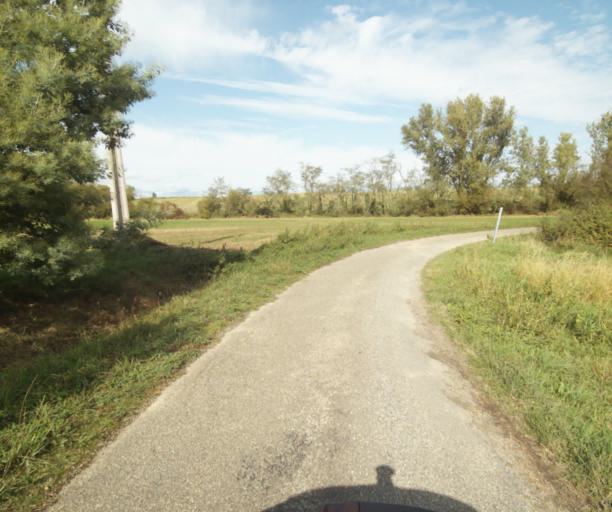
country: FR
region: Midi-Pyrenees
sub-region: Departement du Tarn-et-Garonne
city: Verdun-sur-Garonne
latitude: 43.8634
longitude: 1.1761
